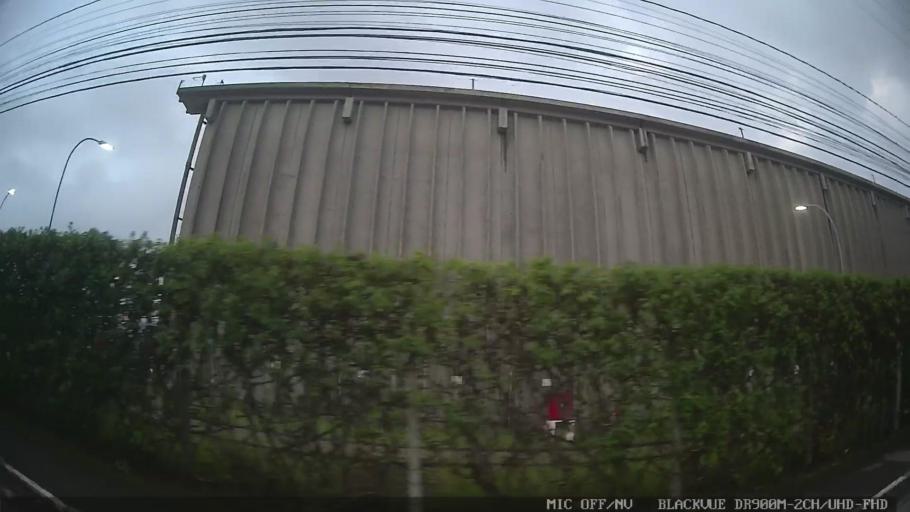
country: BR
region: Sao Paulo
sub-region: Suzano
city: Suzano
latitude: -23.5351
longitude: -46.2916
